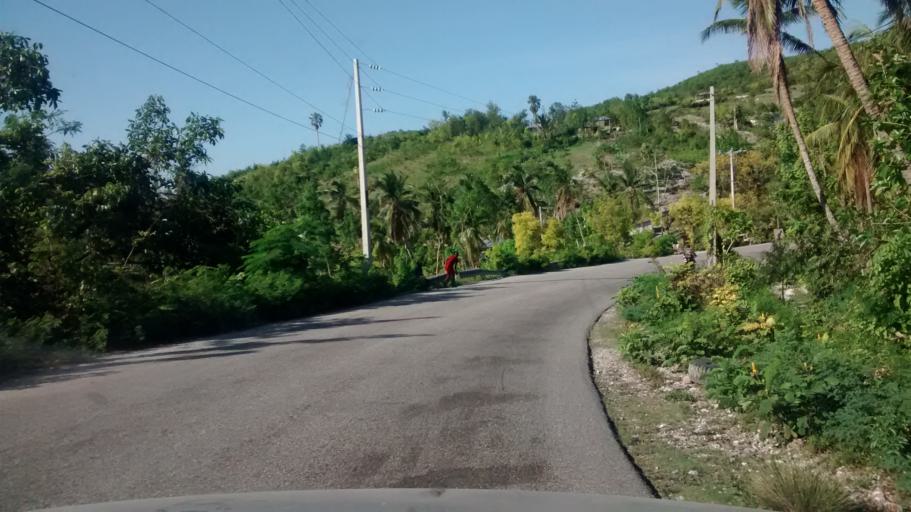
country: HT
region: Sud
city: Cavaillon
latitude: 18.2896
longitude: -73.6366
